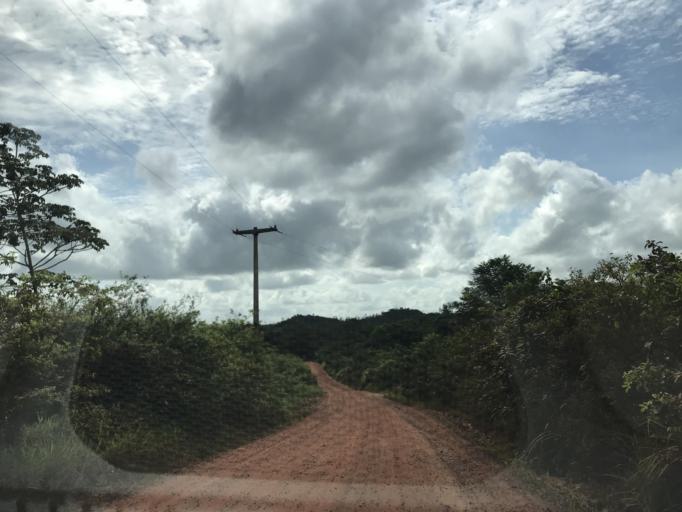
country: BR
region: Bahia
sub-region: Entre Rios
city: Entre Rios
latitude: -12.1702
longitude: -38.1509
